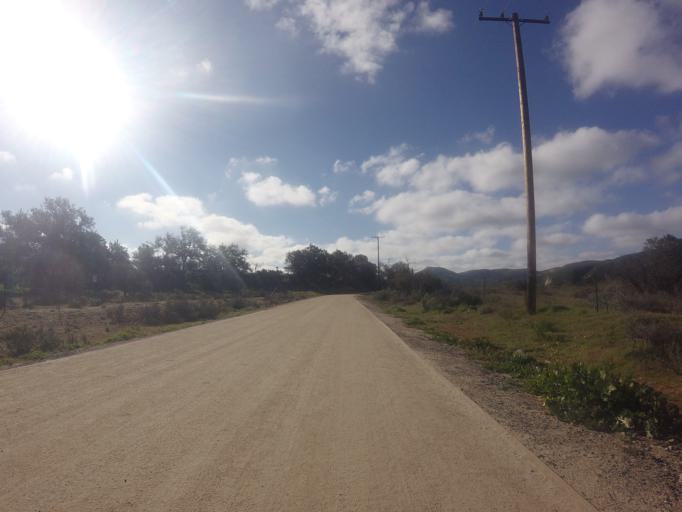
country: US
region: California
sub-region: Orange County
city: Foothill Ranch
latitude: 33.7661
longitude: -117.6783
